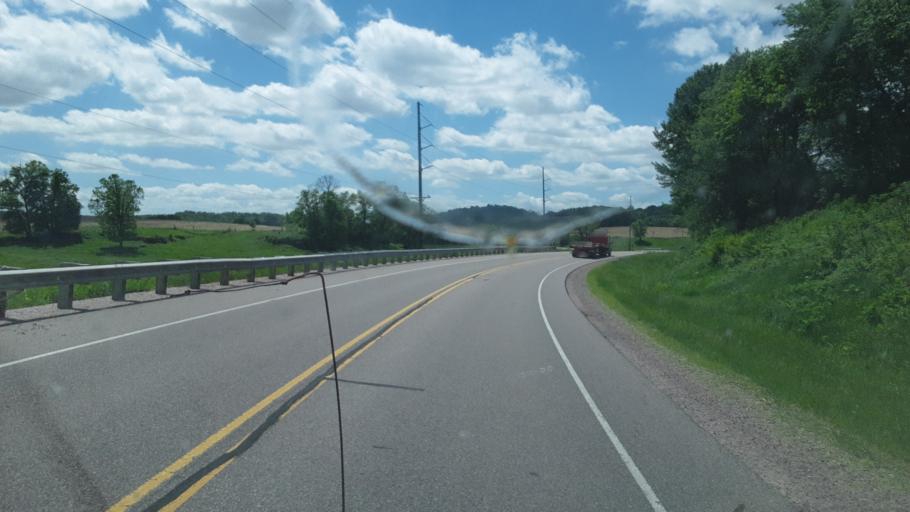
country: US
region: Wisconsin
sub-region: Sauk County
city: Reedsburg
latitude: 43.5757
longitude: -89.9626
